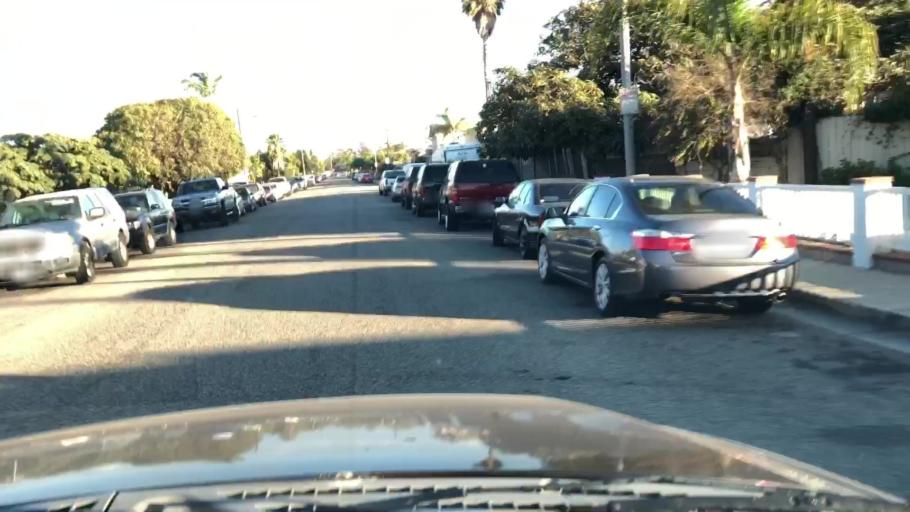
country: US
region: California
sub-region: Ventura County
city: Oxnard
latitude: 34.1860
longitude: -119.1745
